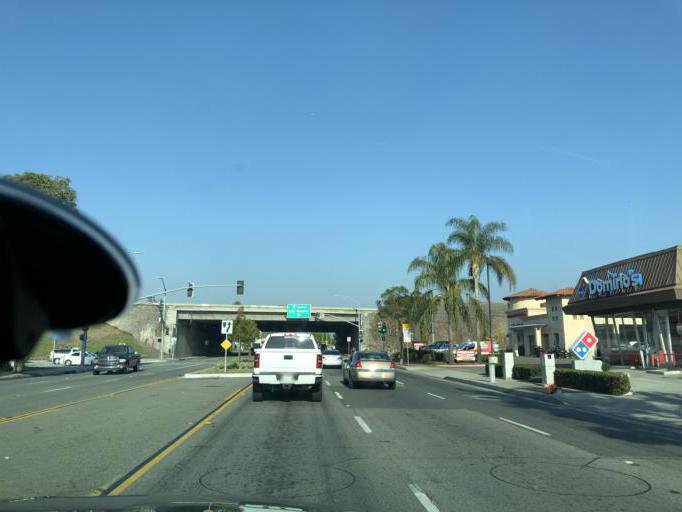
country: US
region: California
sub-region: Orange County
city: Tustin
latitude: 33.7362
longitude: -117.8241
